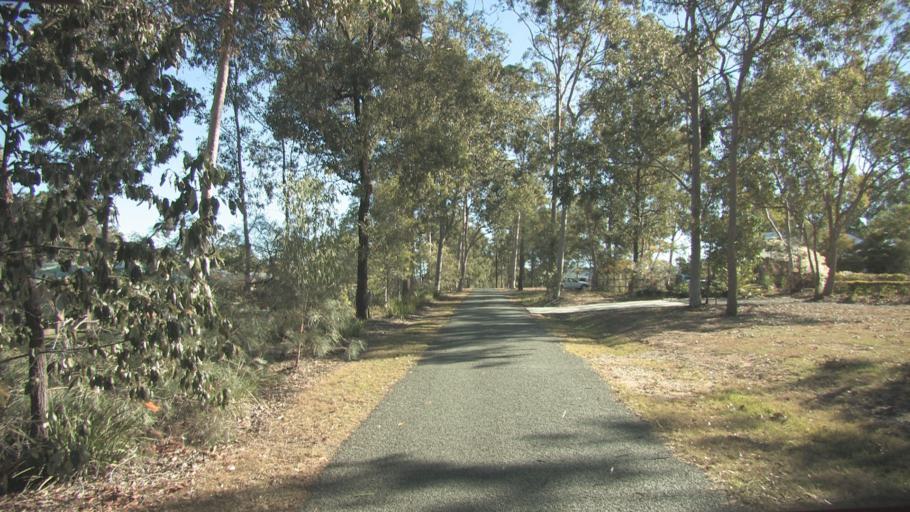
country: AU
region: Queensland
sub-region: Ipswich
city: Springfield Lakes
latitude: -27.7342
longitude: 152.9274
